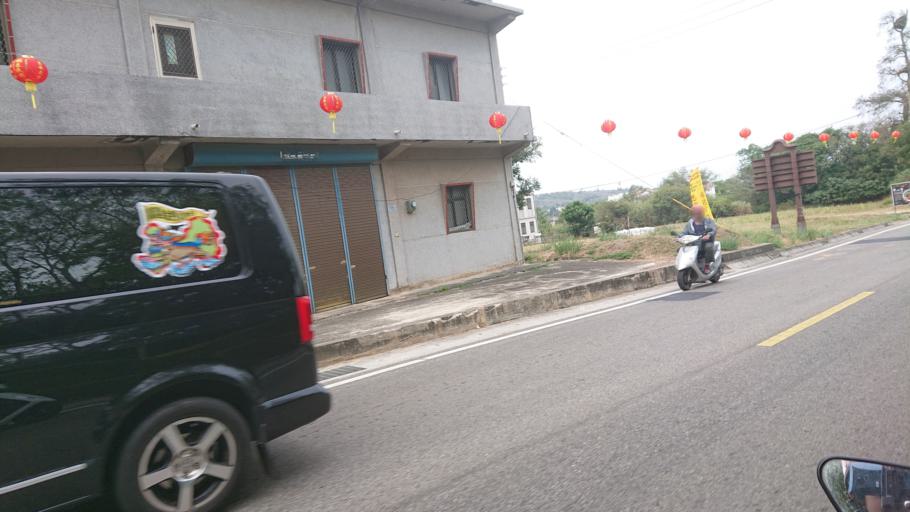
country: TW
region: Fukien
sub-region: Kinmen
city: Jincheng
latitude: 24.4112
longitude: 118.2992
